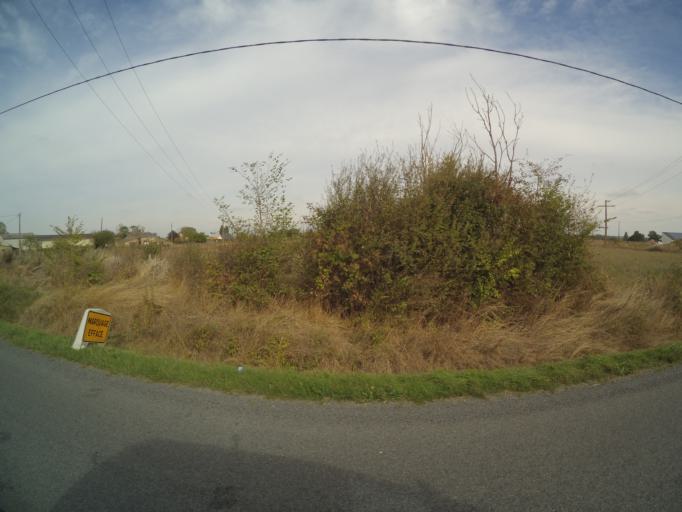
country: FR
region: Pays de la Loire
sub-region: Departement de Maine-et-Loire
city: Martigne-Briand
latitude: 47.2070
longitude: -0.4661
